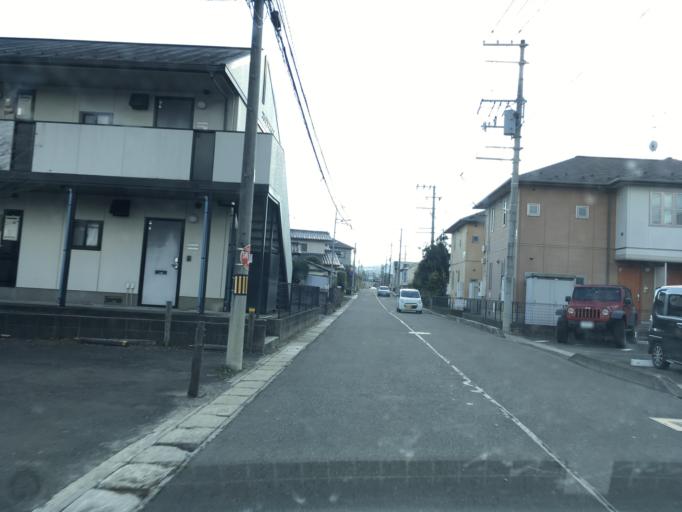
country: JP
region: Miyagi
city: Sendai
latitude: 38.2767
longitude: 140.7645
